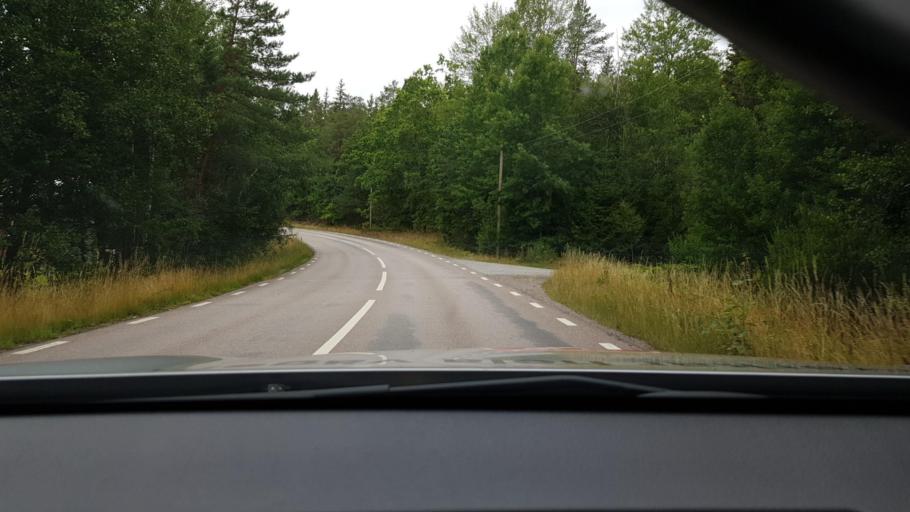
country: SE
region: Soedermanland
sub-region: Strangnas Kommun
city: Mariefred
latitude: 59.1983
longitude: 17.1890
